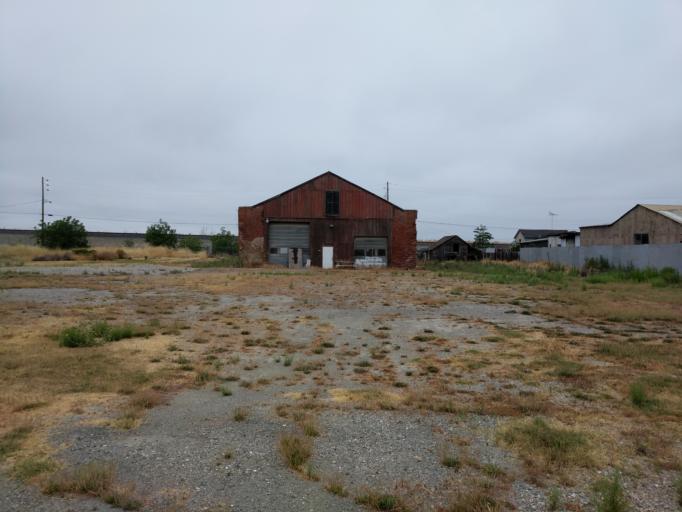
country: US
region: California
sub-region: Santa Clara County
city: Milpitas
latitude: 37.4246
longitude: -121.9762
